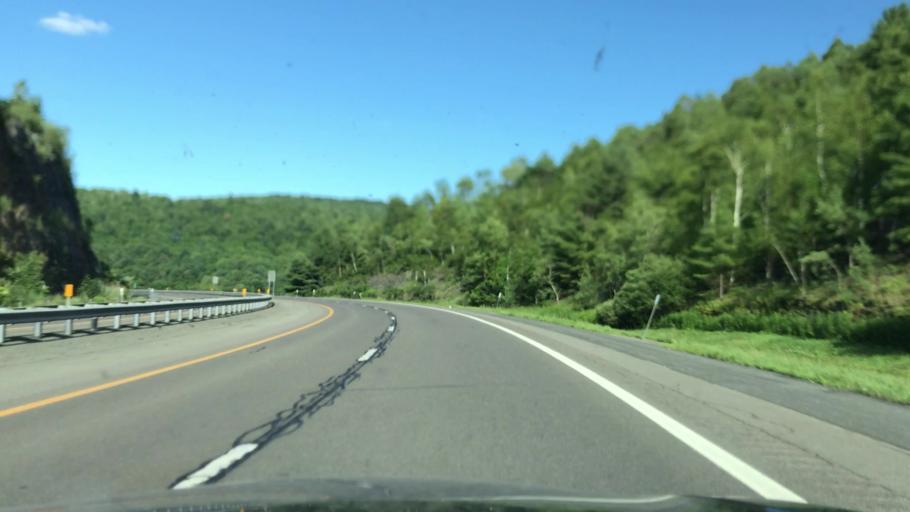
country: US
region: New York
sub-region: Delaware County
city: Hancock
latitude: 41.9558
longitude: -75.2413
